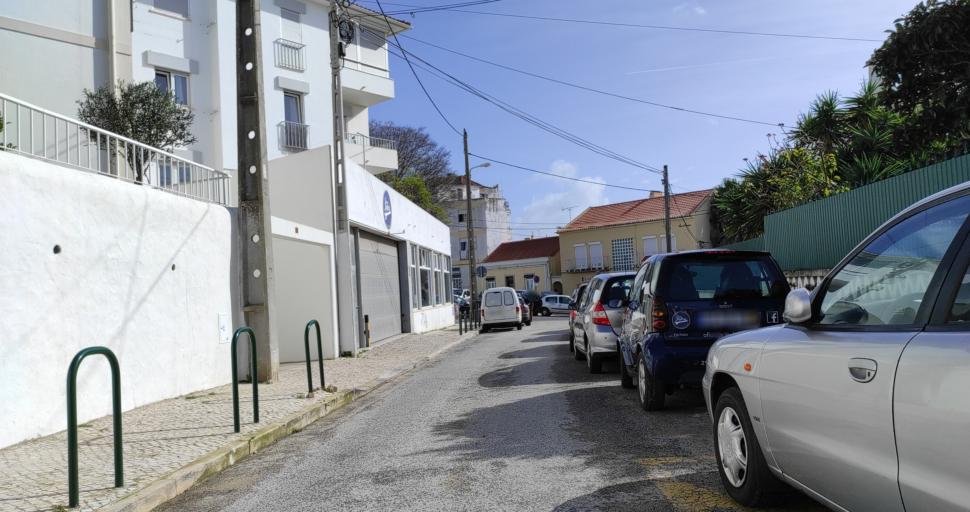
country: PT
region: Lisbon
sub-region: Cascais
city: Parede
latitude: 38.6914
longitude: -9.3543
